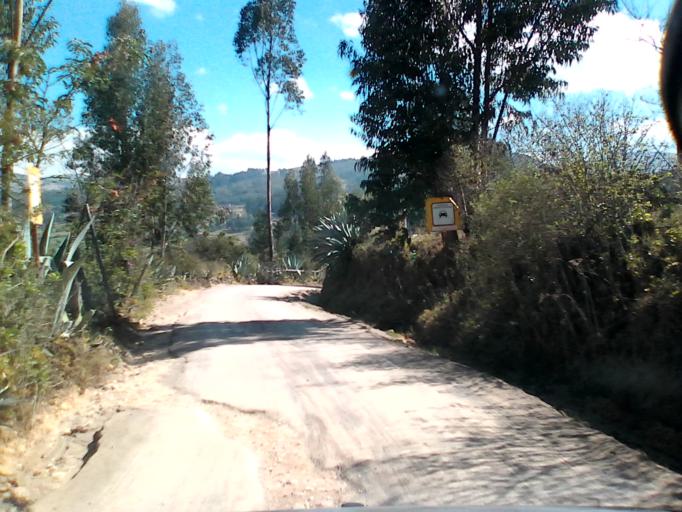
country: CO
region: Boyaca
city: Tibasosa
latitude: 5.7803
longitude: -73.0225
